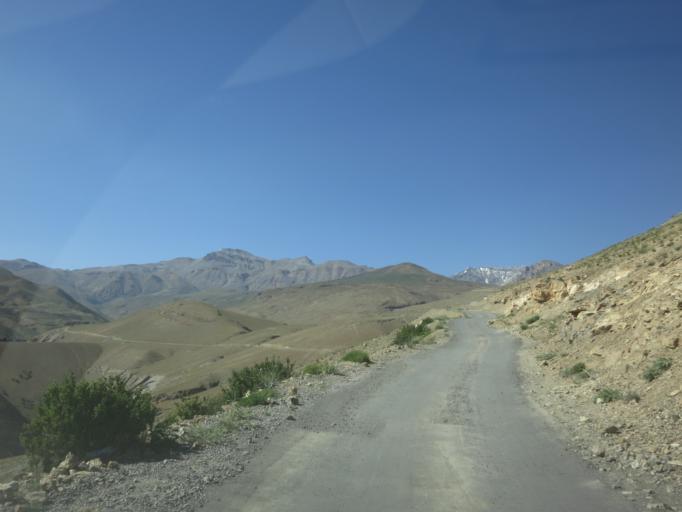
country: IN
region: Himachal Pradesh
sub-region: Kulu
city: Manali
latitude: 32.3233
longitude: 78.0031
